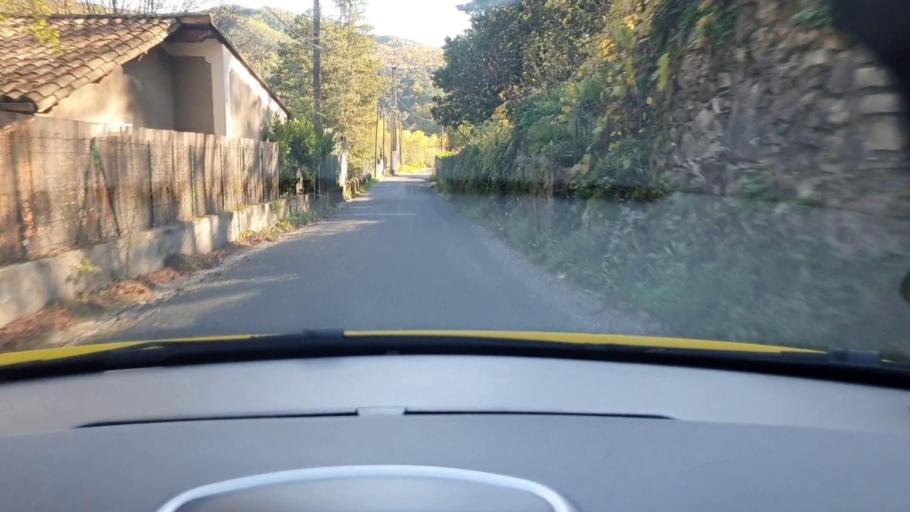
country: FR
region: Languedoc-Roussillon
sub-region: Departement du Gard
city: Le Vigan
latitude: 43.9941
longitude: 3.6208
